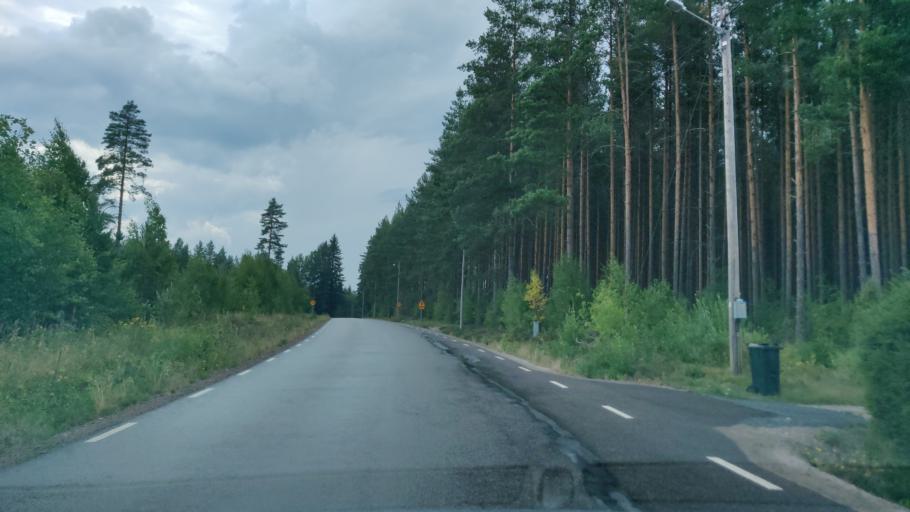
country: SE
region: Vaermland
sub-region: Munkfors Kommun
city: Munkfors
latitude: 59.8670
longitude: 13.5430
